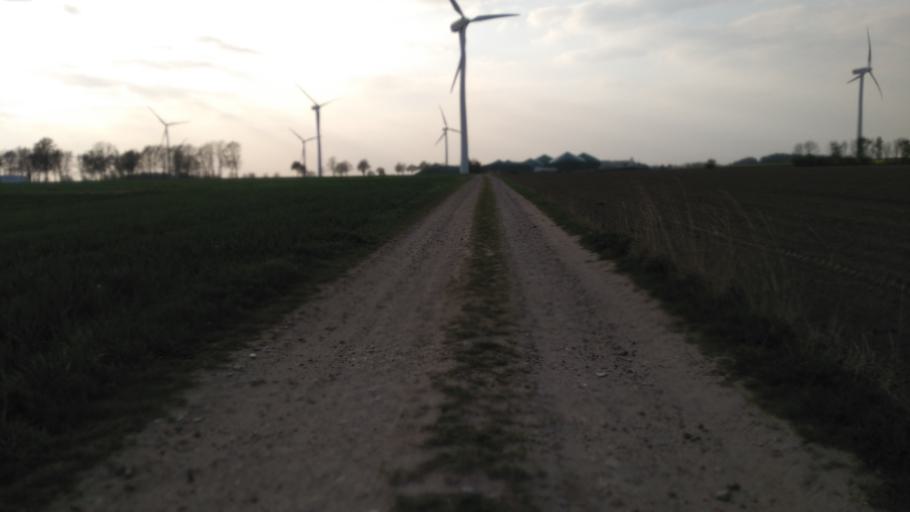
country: DE
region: Lower Saxony
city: Apensen
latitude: 53.4561
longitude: 9.6074
